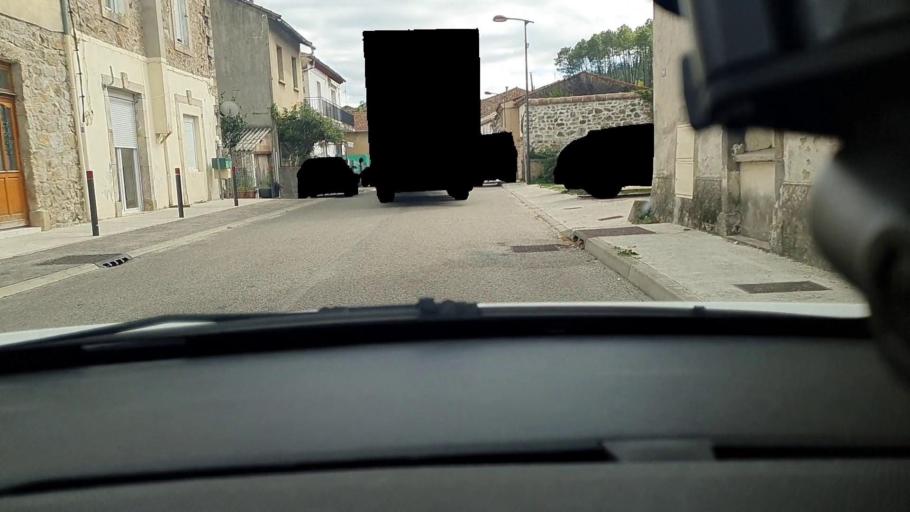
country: FR
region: Languedoc-Roussillon
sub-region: Departement du Gard
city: Saint-Florent-sur-Auzonnet
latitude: 44.2547
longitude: 4.0835
